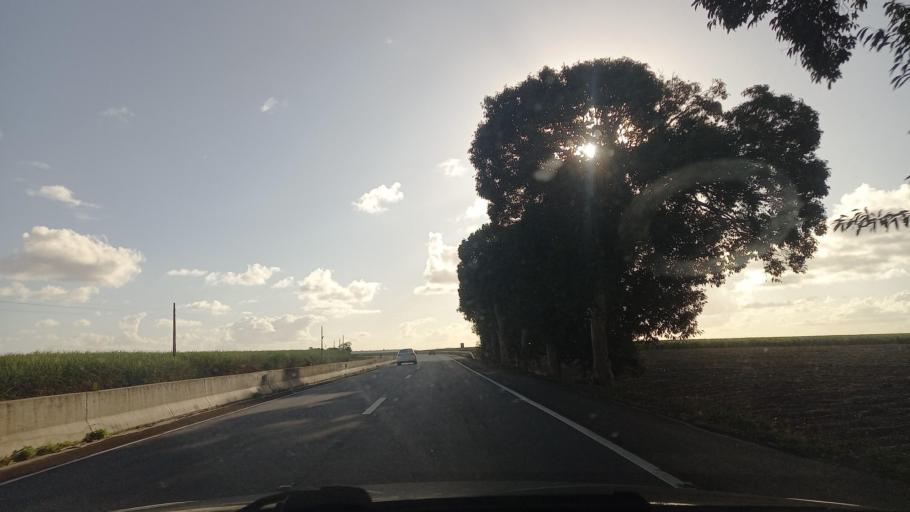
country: BR
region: Alagoas
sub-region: Sao Miguel Dos Campos
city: Sao Miguel dos Campos
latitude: -9.8000
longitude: -36.1633
